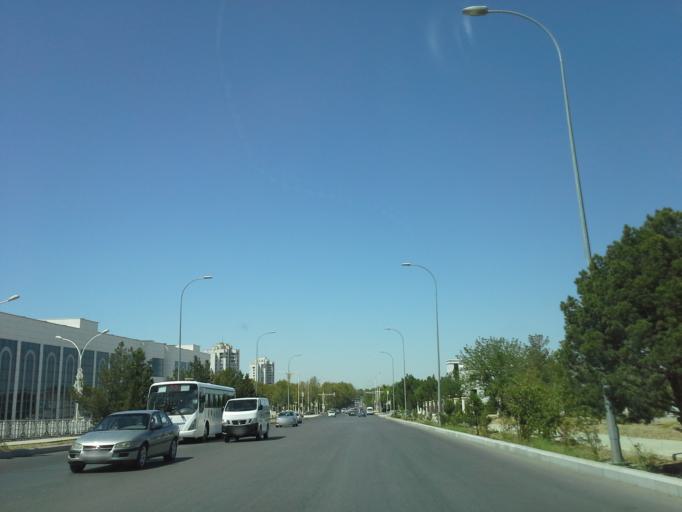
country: TM
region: Ahal
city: Ashgabat
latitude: 37.9081
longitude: 58.4059
